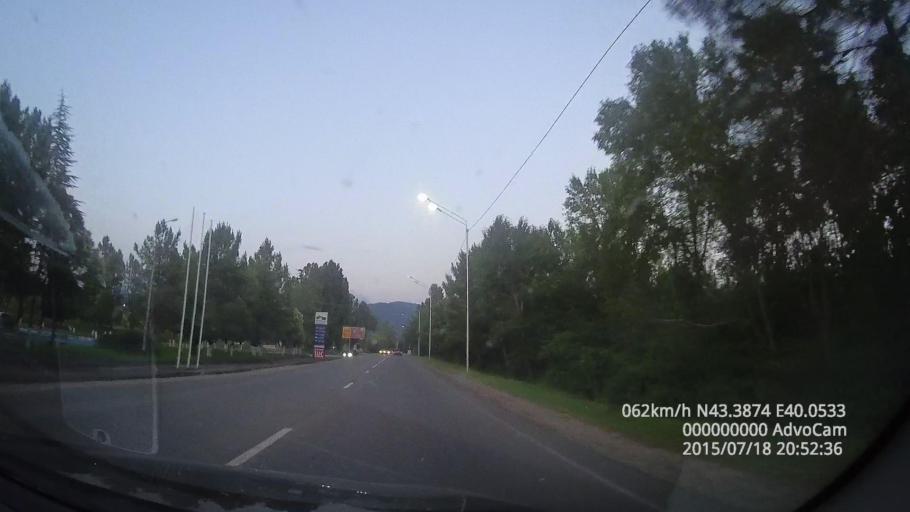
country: GE
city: Gantiadi
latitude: 43.3872
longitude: 40.0548
